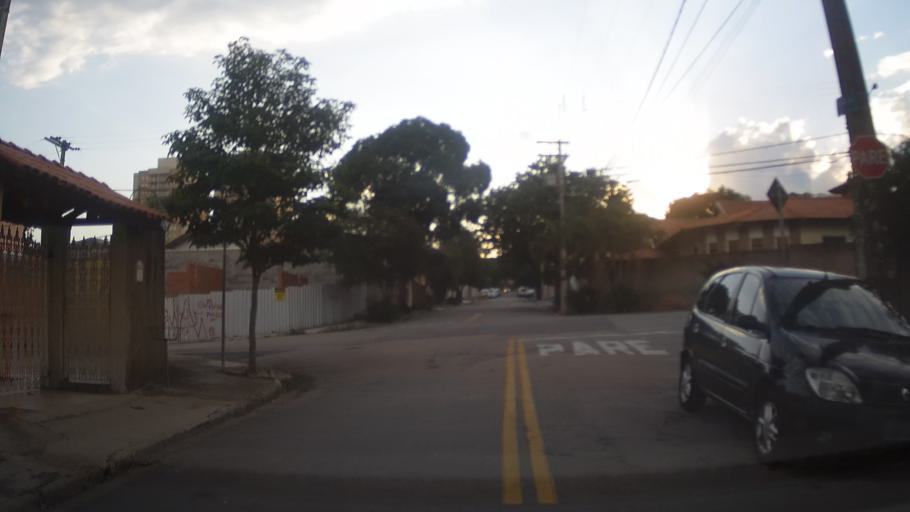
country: BR
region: Sao Paulo
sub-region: Jundiai
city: Jundiai
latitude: -23.1883
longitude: -46.9625
